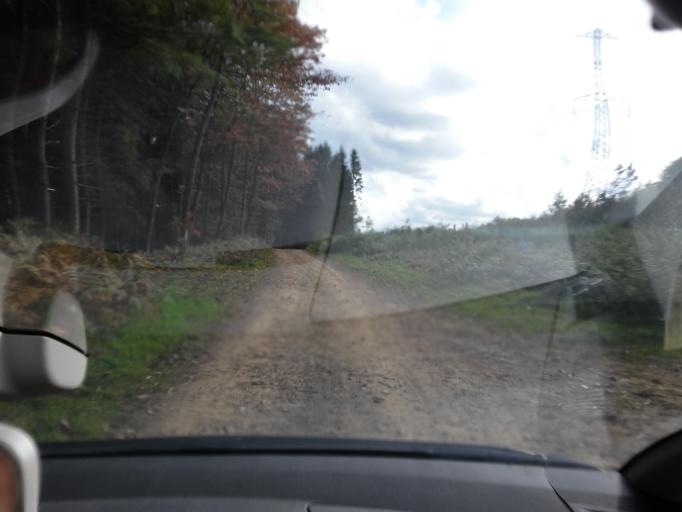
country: BE
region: Wallonia
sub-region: Province du Luxembourg
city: Attert
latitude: 49.7065
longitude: 5.7617
